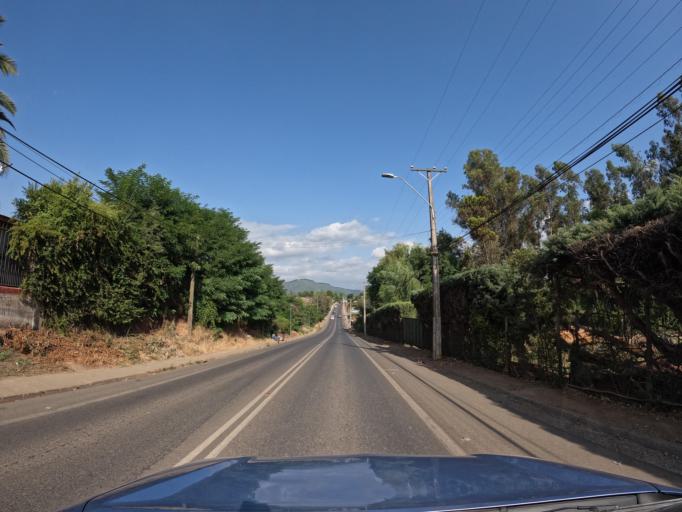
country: CL
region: Maule
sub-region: Provincia de Curico
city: Molina
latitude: -35.2810
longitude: -71.2633
